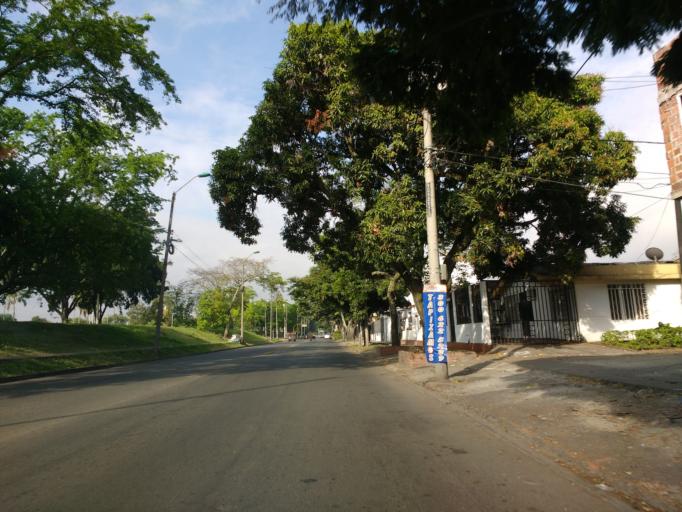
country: CO
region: Valle del Cauca
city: Cali
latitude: 3.4763
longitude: -76.5135
